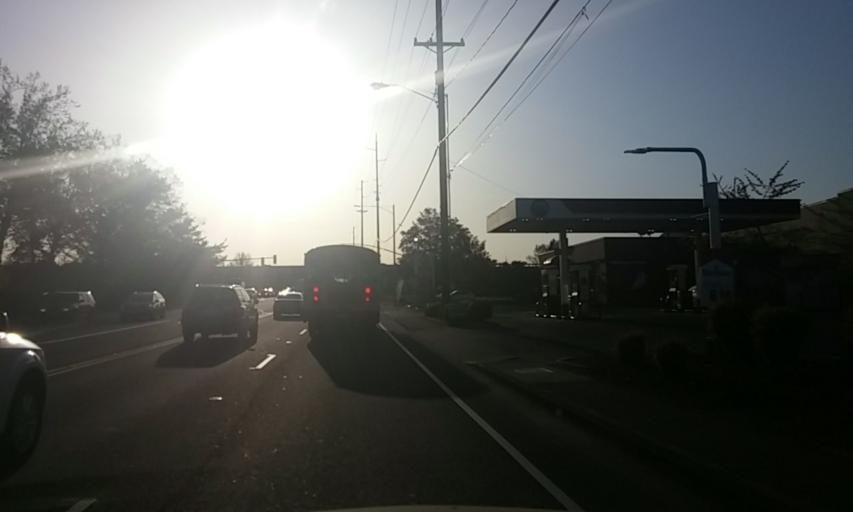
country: US
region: Oregon
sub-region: Washington County
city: Beaverton
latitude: 45.4864
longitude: -122.7955
